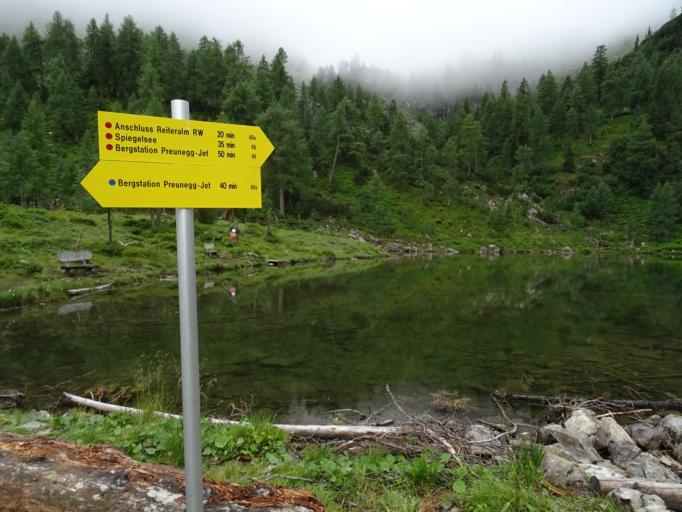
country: AT
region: Salzburg
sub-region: Politischer Bezirk Sankt Johann im Pongau
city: Forstau
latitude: 47.3515
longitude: 13.5992
